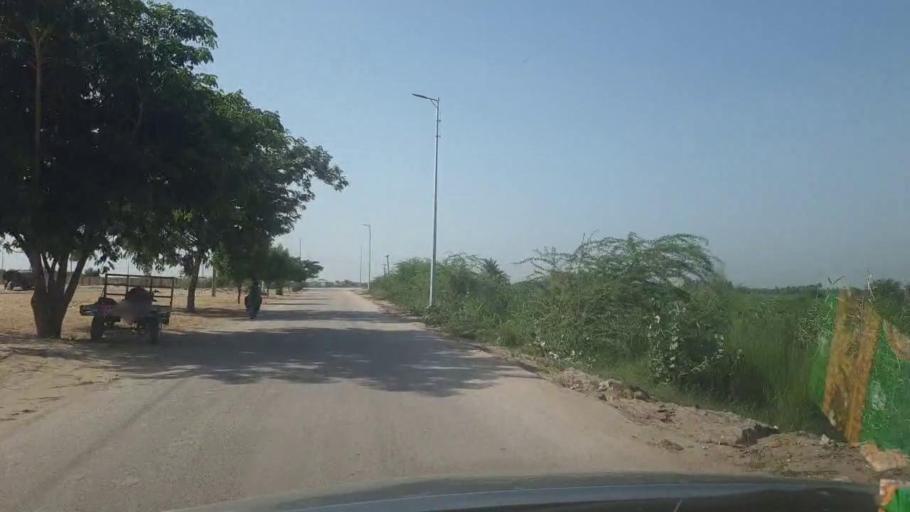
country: PK
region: Sindh
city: Rohri
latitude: 27.5066
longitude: 69.0369
